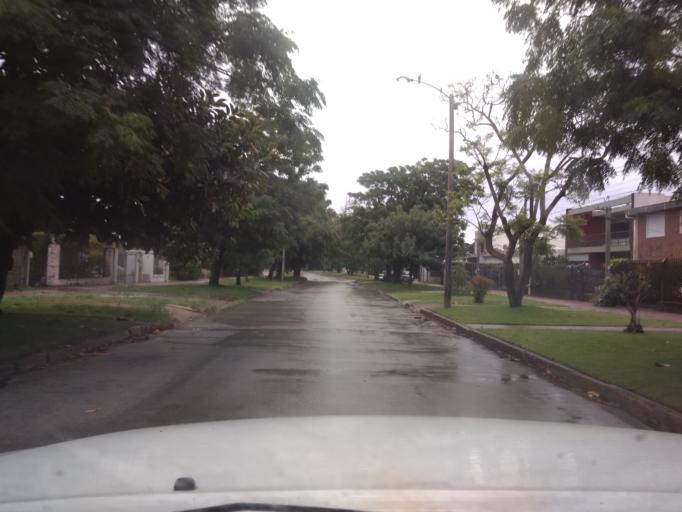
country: UY
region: Canelones
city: Paso de Carrasco
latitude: -34.8927
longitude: -56.0689
